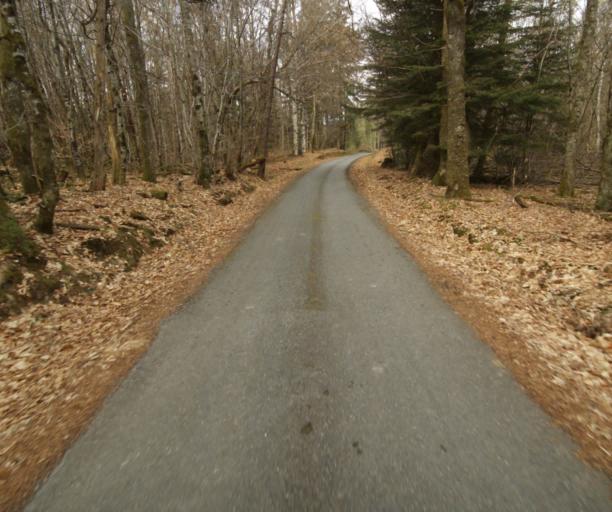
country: FR
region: Limousin
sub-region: Departement de la Correze
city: Argentat
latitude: 45.1908
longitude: 1.9290
